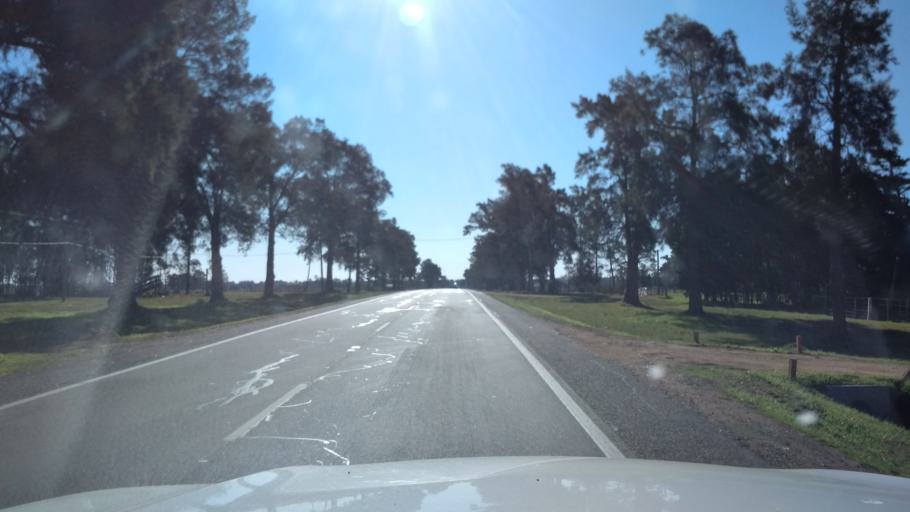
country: UY
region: Canelones
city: San Jacinto
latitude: -34.5787
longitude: -55.8458
